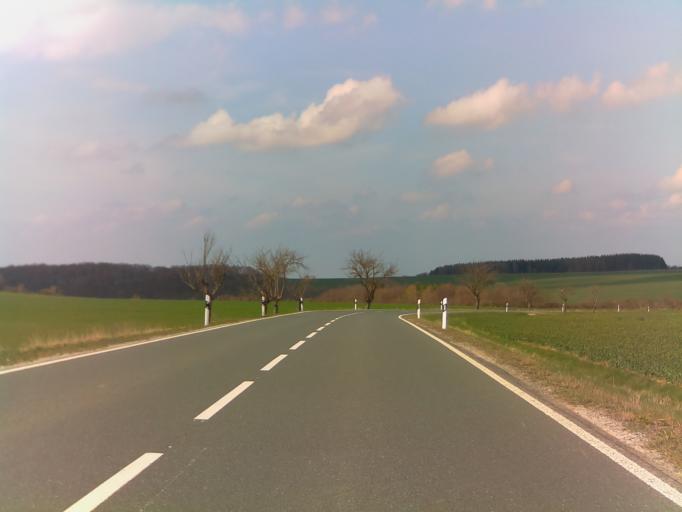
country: DE
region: Thuringia
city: Milda
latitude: 50.8630
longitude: 11.4569
